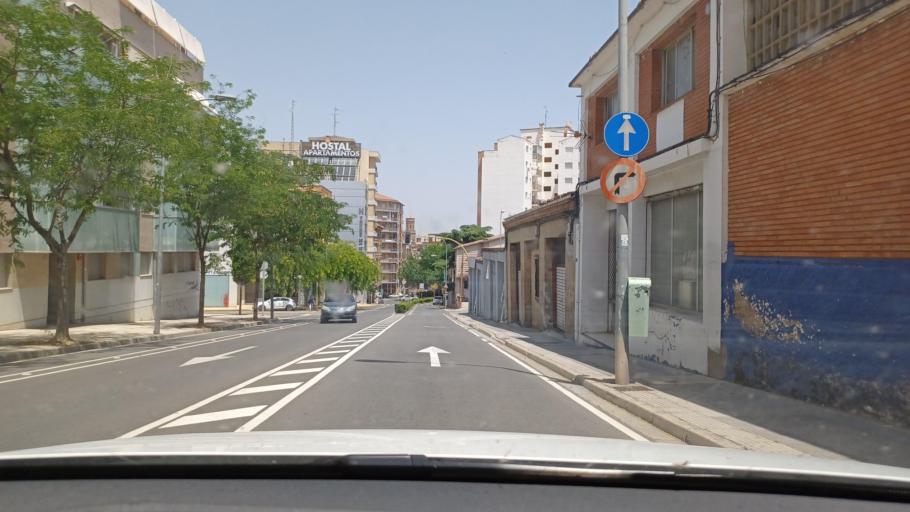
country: ES
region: Navarre
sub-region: Provincia de Navarra
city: Tudela
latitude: 42.0580
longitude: -1.6083
